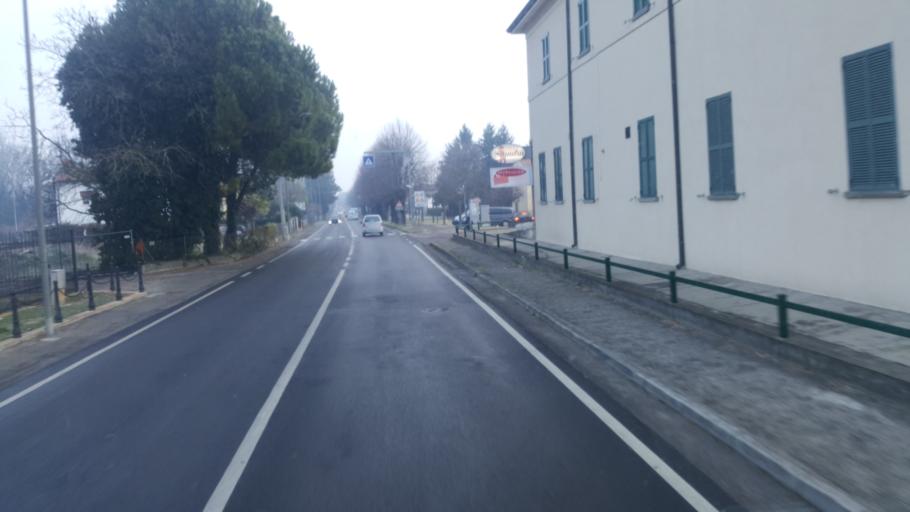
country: IT
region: Emilia-Romagna
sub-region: Provincia di Ravenna
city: Bagnacavallo
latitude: 44.4091
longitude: 11.9695
